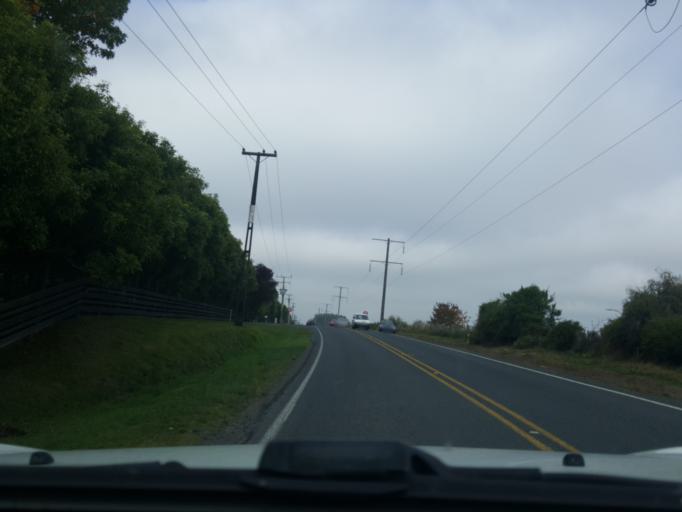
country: NZ
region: Waikato
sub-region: Hamilton City
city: Hamilton
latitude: -37.7401
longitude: 175.2894
